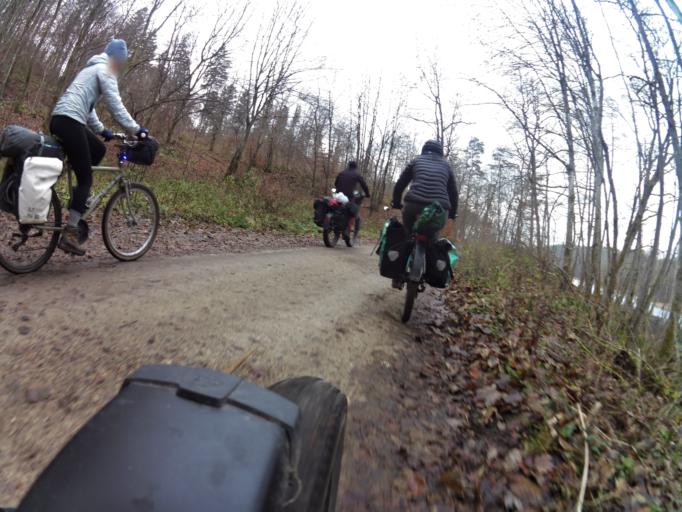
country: PL
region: West Pomeranian Voivodeship
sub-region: Powiat koszalinski
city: Polanow
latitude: 54.0589
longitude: 16.6697
